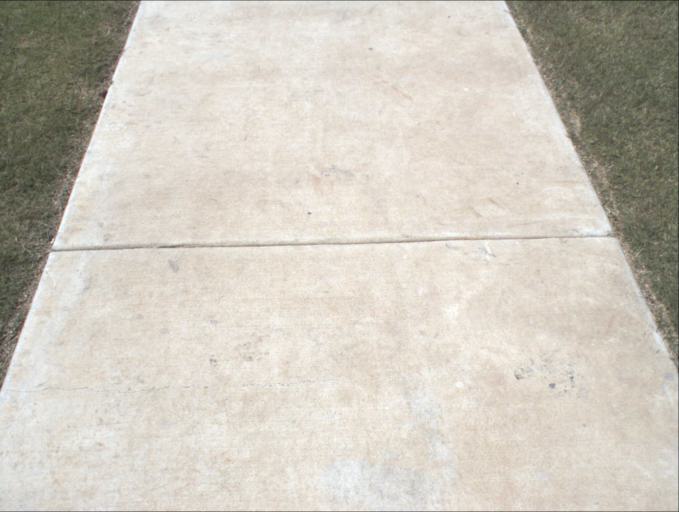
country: AU
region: Queensland
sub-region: Logan
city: Chambers Flat
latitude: -27.8070
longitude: 153.1132
